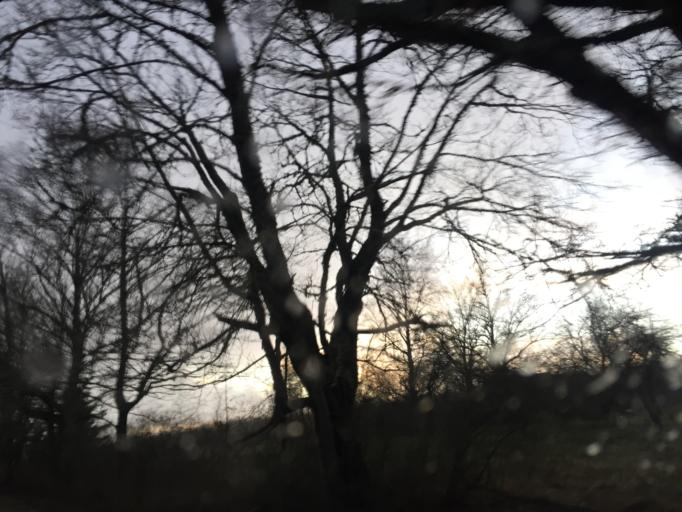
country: LV
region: Burtnieki
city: Matisi
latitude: 57.6824
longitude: 25.2432
